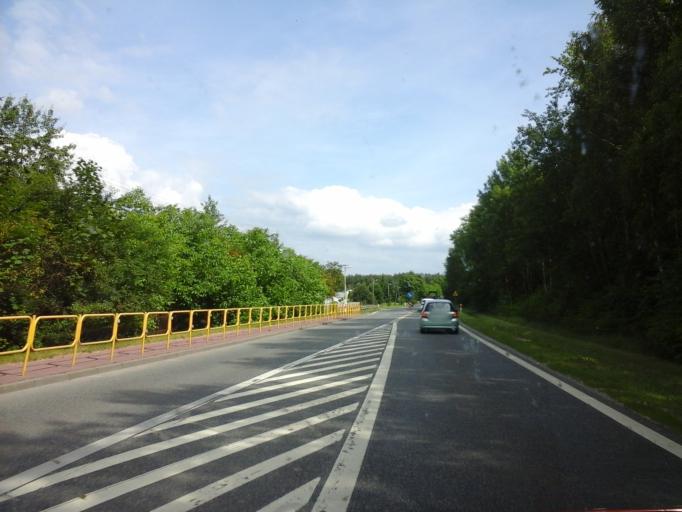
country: PL
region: Lodz Voivodeship
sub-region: Powiat opoczynski
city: Paradyz
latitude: 51.2982
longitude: 20.1203
